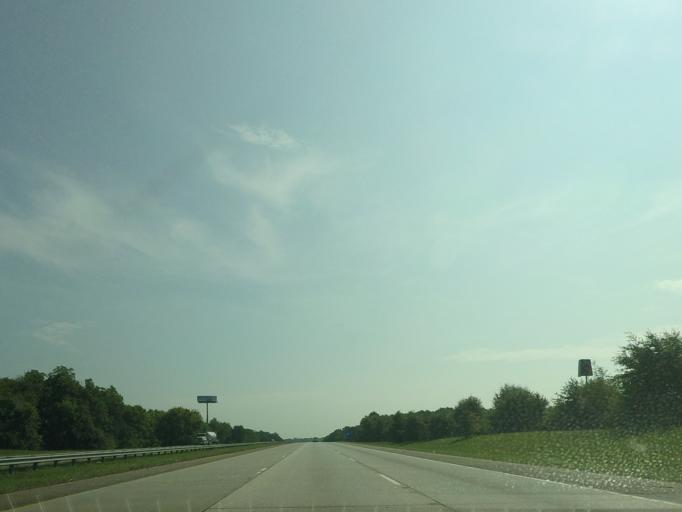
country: US
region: Georgia
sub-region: Bibb County
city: Macon
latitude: 32.7787
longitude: -83.6826
